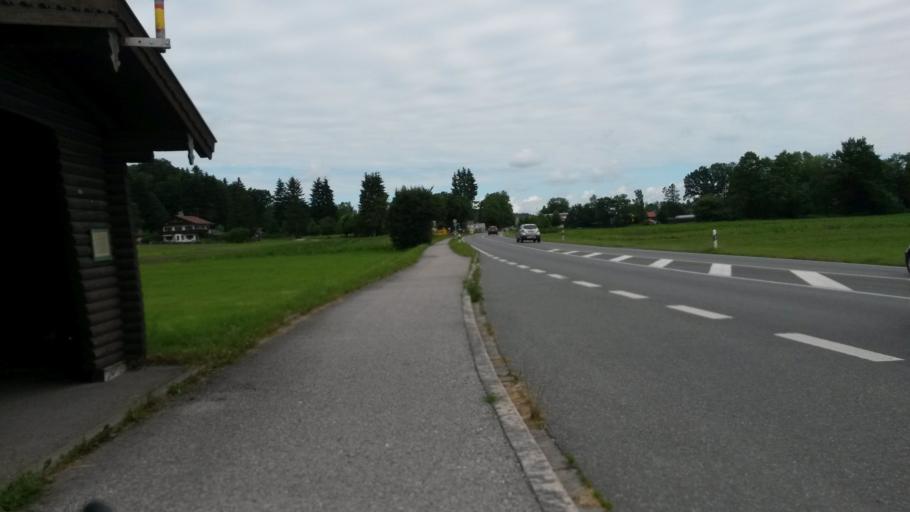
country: DE
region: Bavaria
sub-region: Upper Bavaria
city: Prien am Chiemsee
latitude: 47.8343
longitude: 12.3541
